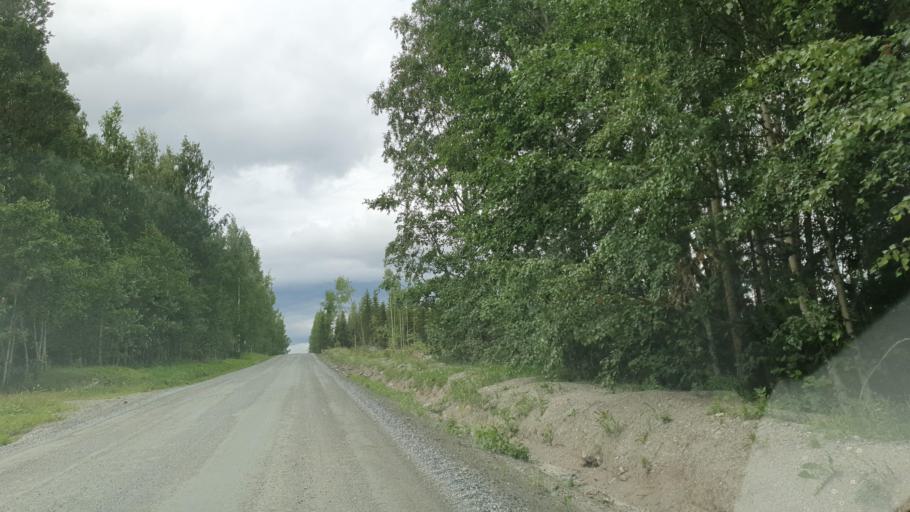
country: FI
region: Northern Savo
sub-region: Ylae-Savo
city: Iisalmi
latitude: 63.5228
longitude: 27.0949
